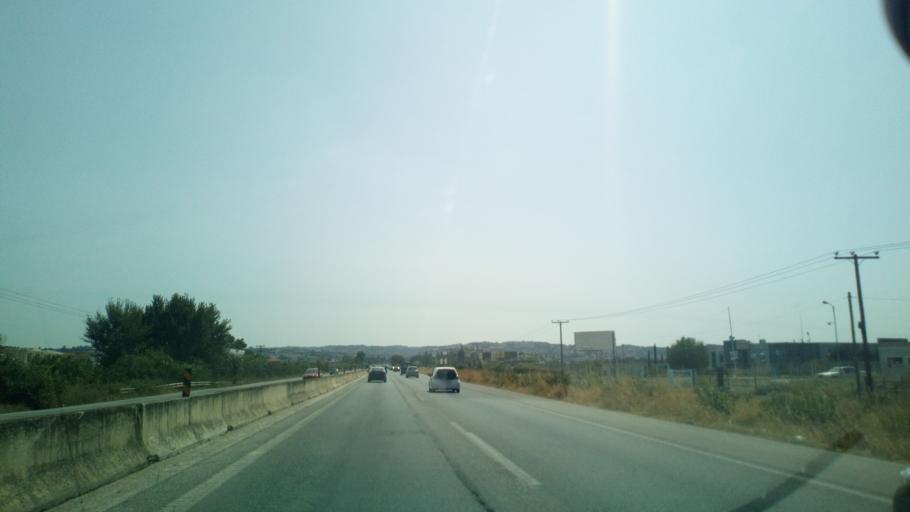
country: GR
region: Central Macedonia
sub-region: Nomos Thessalonikis
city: Neo Rysi
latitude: 40.5113
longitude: 23.0083
